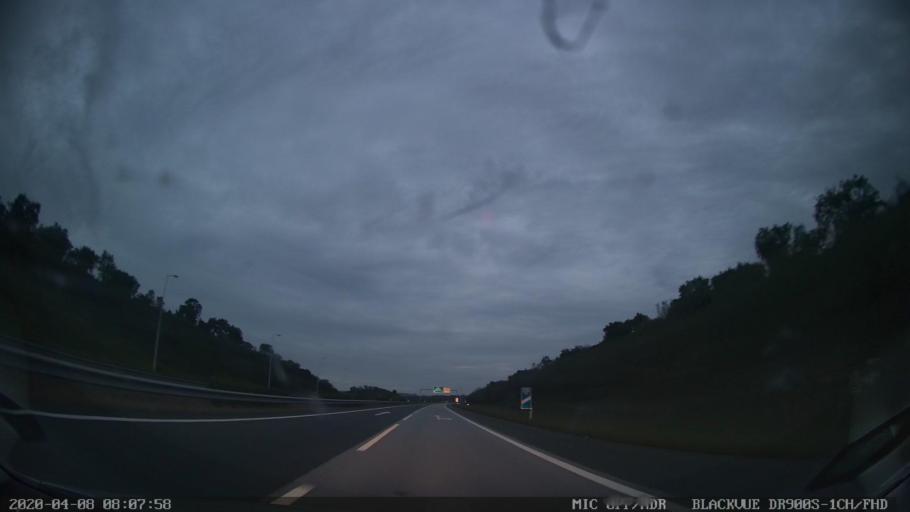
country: PT
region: Evora
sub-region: Evora
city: Evora
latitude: 38.6021
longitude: -8.0193
